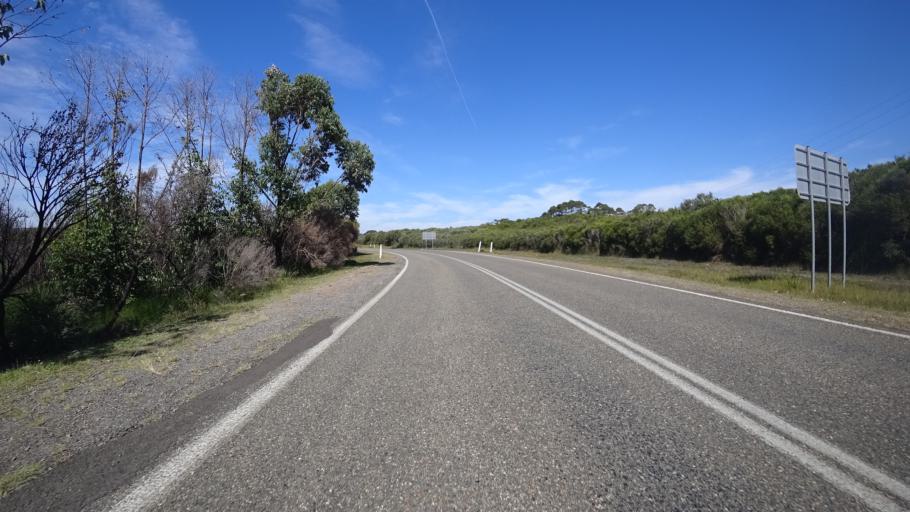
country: AU
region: New South Wales
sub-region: Shoalhaven Shire
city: Falls Creek
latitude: -35.1385
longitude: 150.7049
